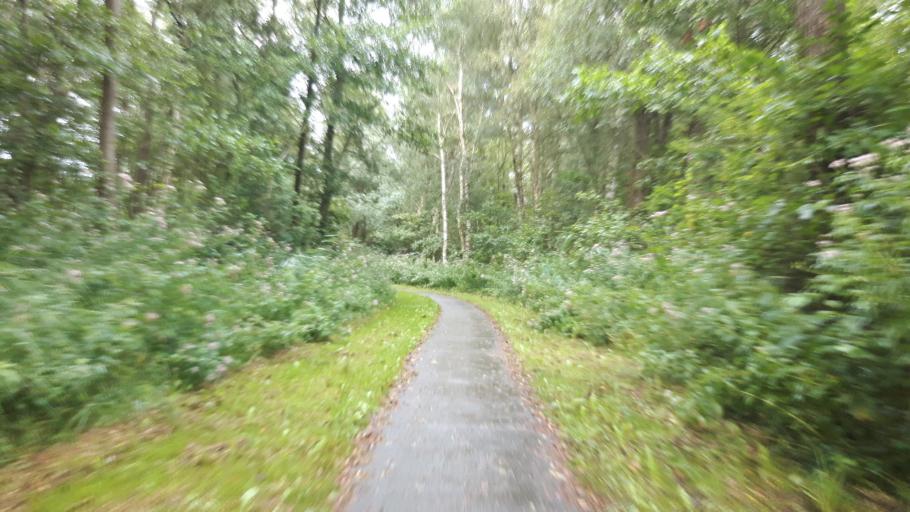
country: NL
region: Overijssel
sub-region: Gemeente Steenwijkerland
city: Blokzijl
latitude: 52.7677
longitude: 5.9619
